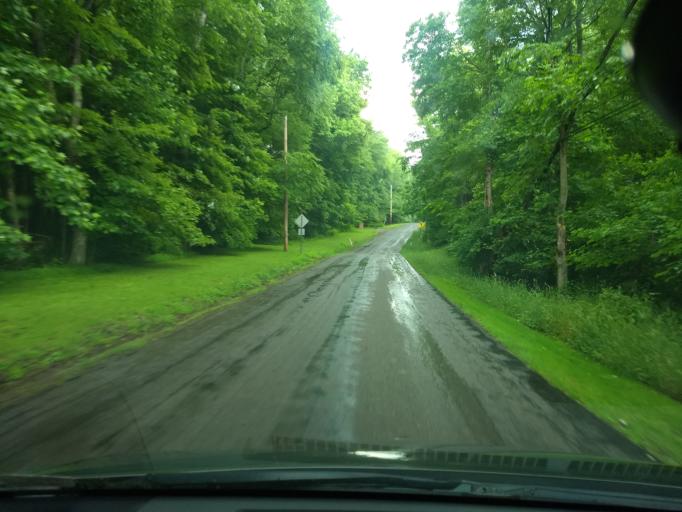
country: US
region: Pennsylvania
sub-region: Westmoreland County
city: Avonmore
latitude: 40.5365
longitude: -79.4921
